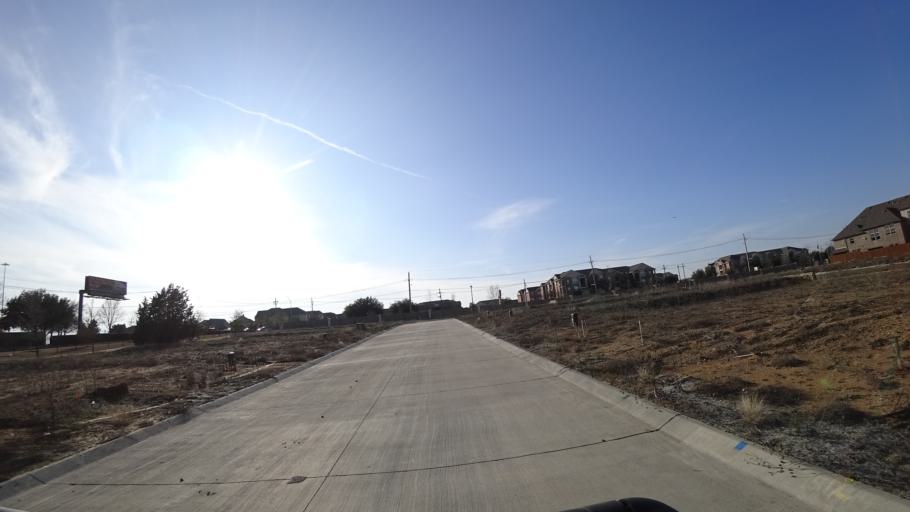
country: US
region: Texas
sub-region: Denton County
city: Lewisville
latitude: 33.0075
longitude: -96.9919
